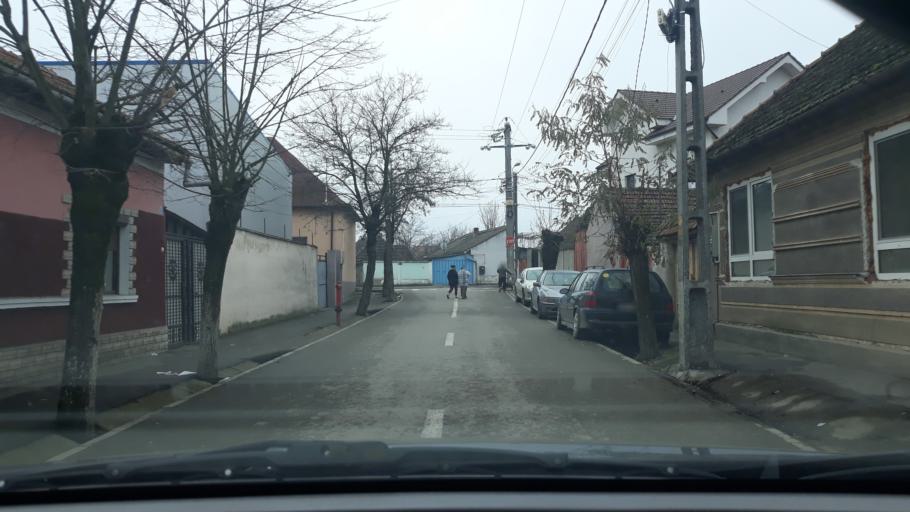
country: RO
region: Bihor
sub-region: Comuna Biharea
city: Oradea
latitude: 47.0476
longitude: 21.9692
